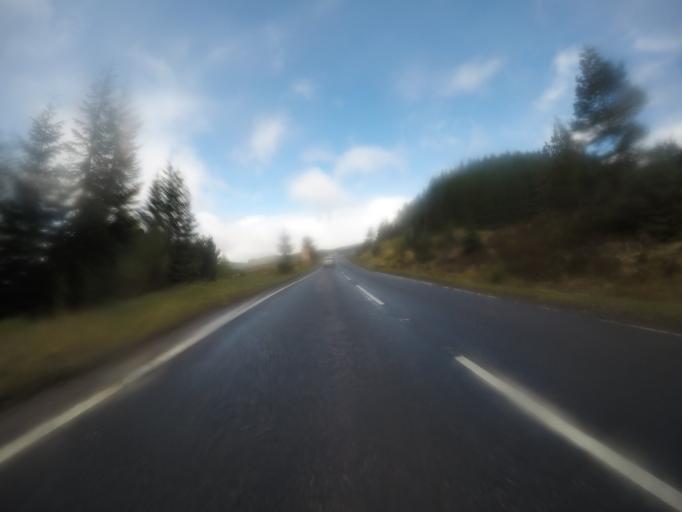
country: GB
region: Scotland
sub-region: Highland
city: Spean Bridge
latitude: 57.0835
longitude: -4.9586
